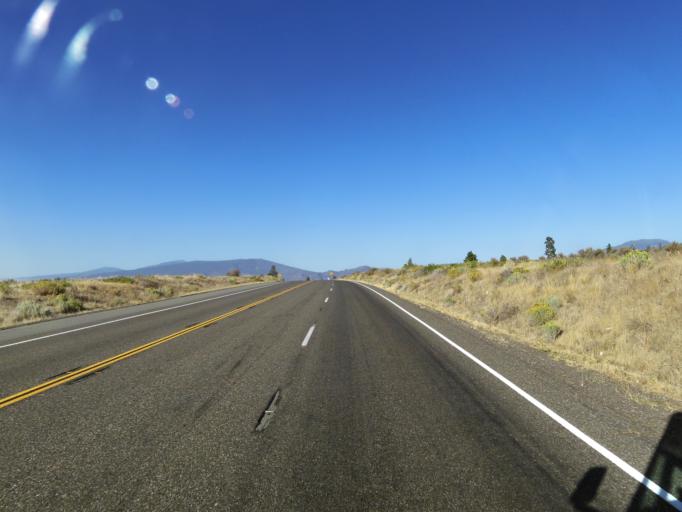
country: US
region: California
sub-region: Siskiyou County
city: Weed
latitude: 41.4813
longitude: -122.3438
